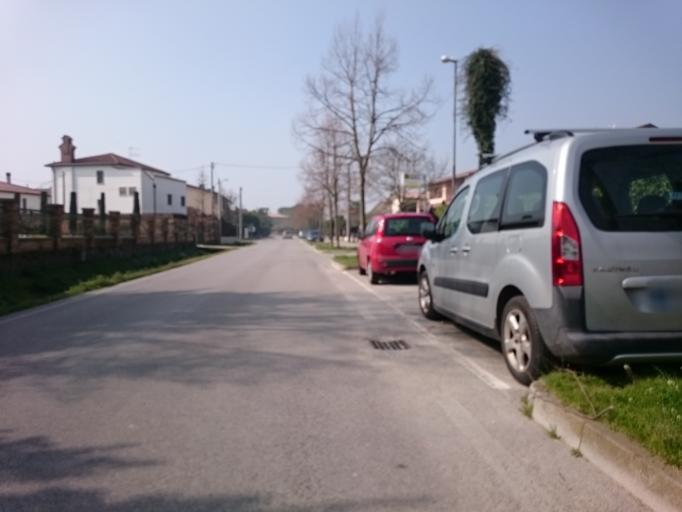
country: IT
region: Veneto
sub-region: Provincia di Padova
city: Pernumia
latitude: 45.2593
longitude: 11.7940
